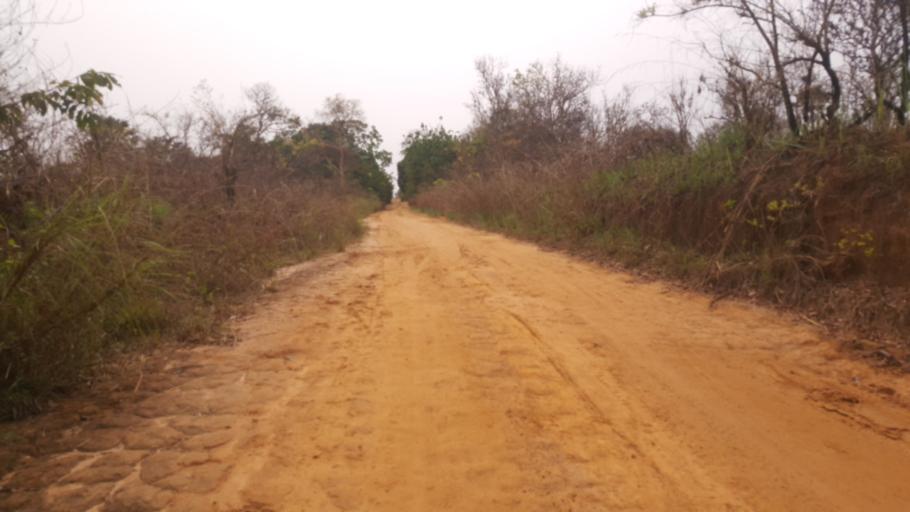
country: CD
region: Bandundu
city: Bandundu
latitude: -3.4553
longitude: 17.7439
